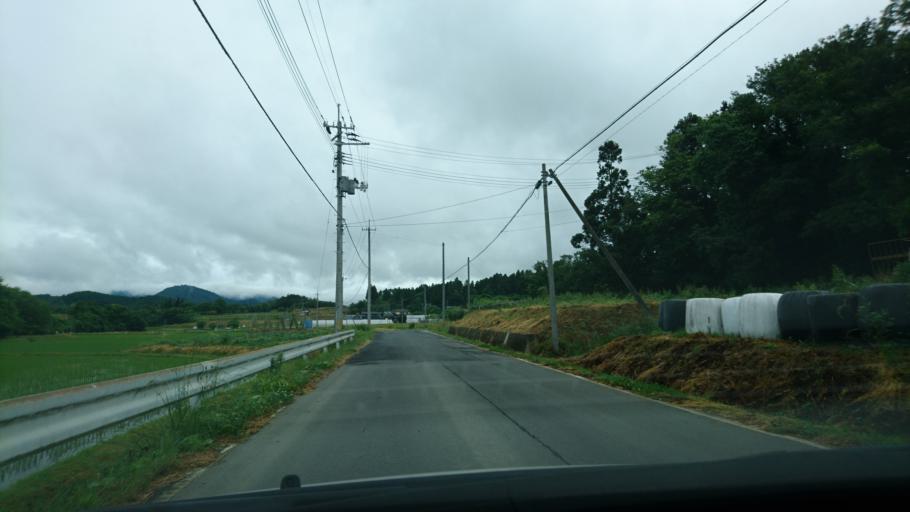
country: JP
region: Iwate
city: Ichinoseki
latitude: 38.9213
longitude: 141.2091
